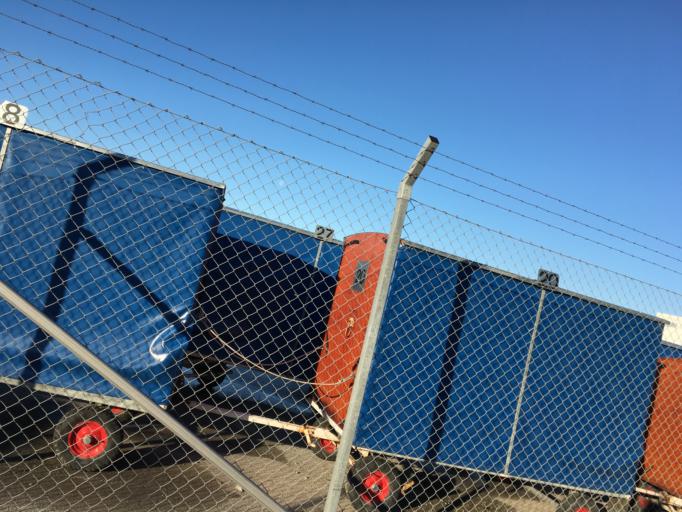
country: SE
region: Gotland
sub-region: Gotland
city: Visby
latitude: 57.6357
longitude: 18.2808
